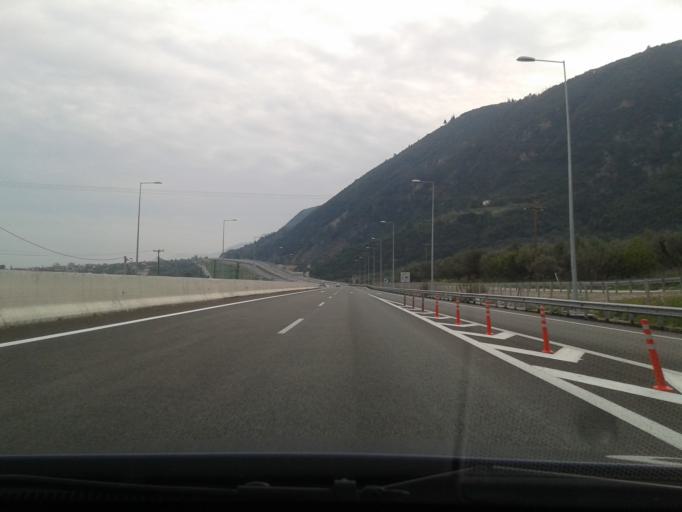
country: GR
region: West Greece
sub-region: Nomos Achaias
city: Temeni
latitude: 38.2194
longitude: 22.1060
